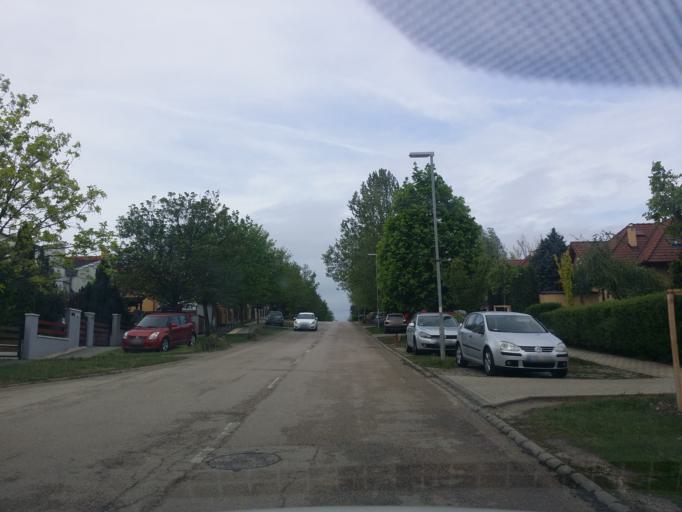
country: HU
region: Pest
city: Biatorbagy
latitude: 47.4833
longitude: 18.8235
